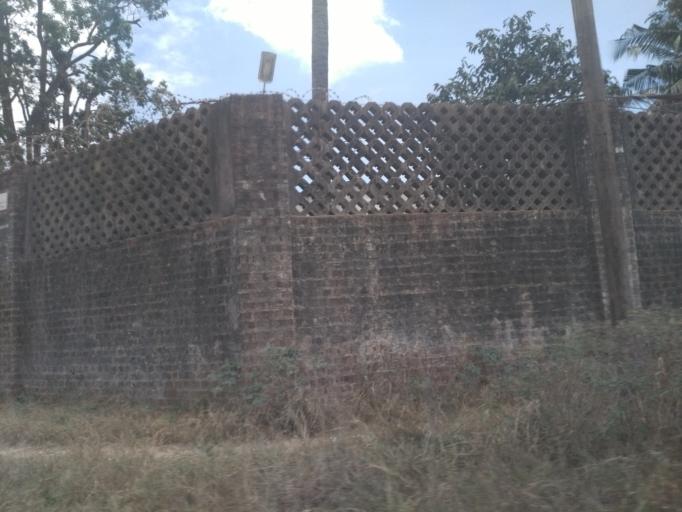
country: TZ
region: Dar es Salaam
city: Dar es Salaam
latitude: -6.8495
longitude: 39.2696
